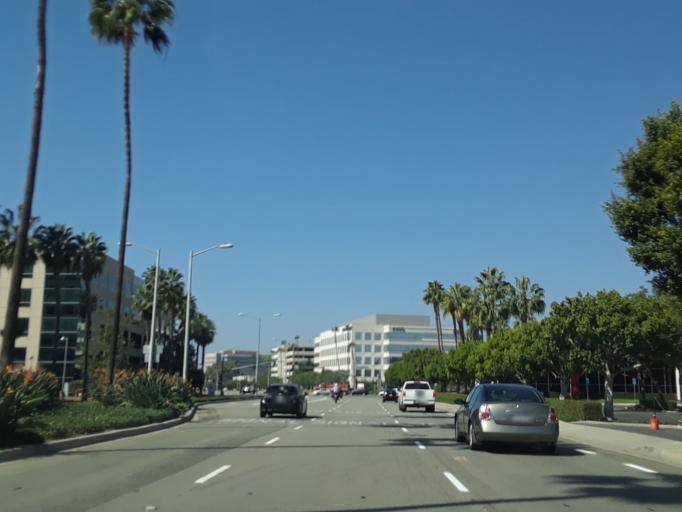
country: US
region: California
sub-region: Orange County
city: Irvine
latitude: 33.6835
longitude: -117.8456
